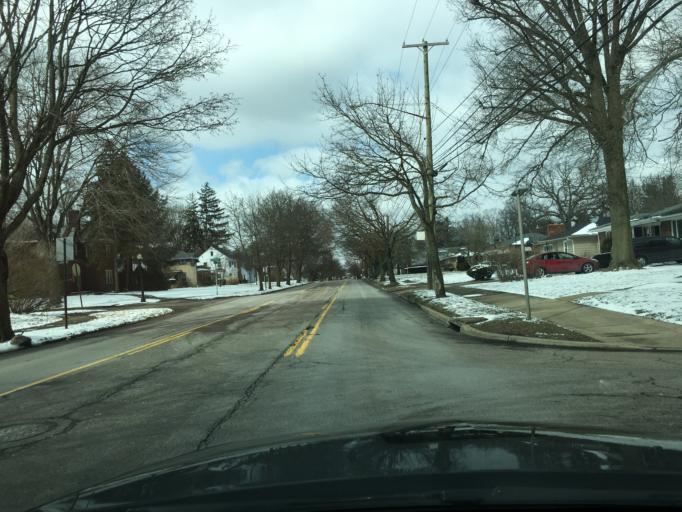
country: US
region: Ohio
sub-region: Summit County
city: Akron
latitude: 41.1048
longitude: -81.5632
